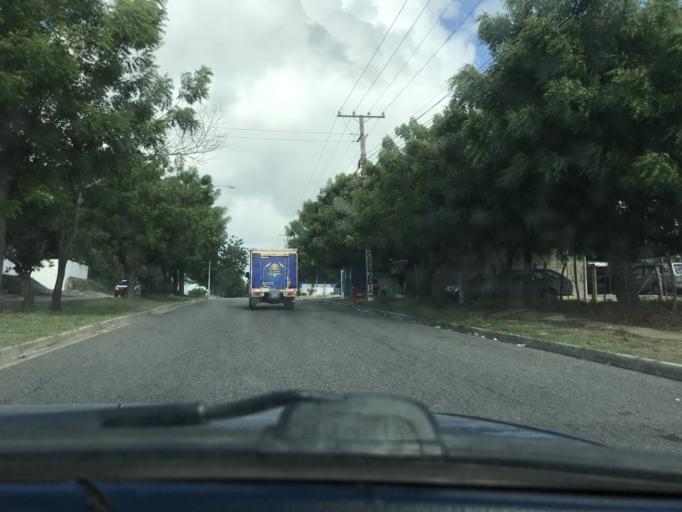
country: DO
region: Santiago
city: Santiago de los Caballeros
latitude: 19.4138
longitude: -70.7244
